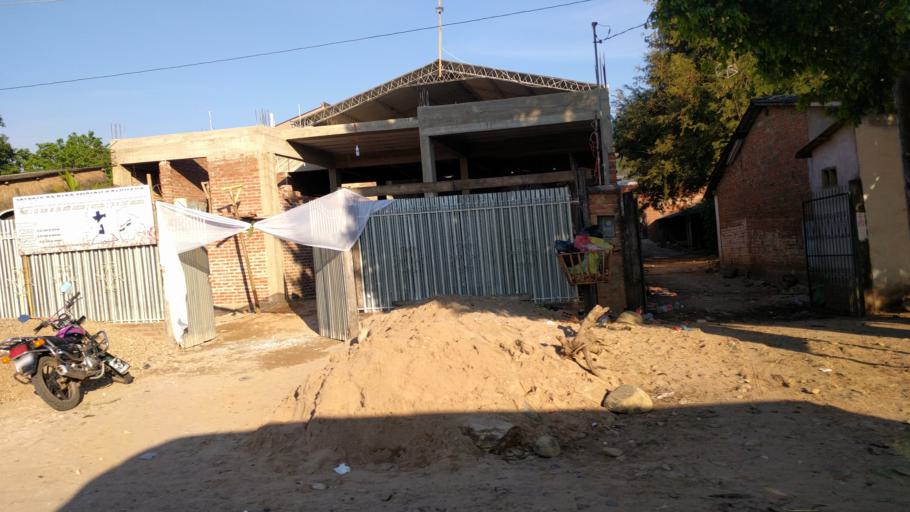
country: BO
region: Santa Cruz
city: Santiago del Torno
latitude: -17.9992
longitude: -63.3864
